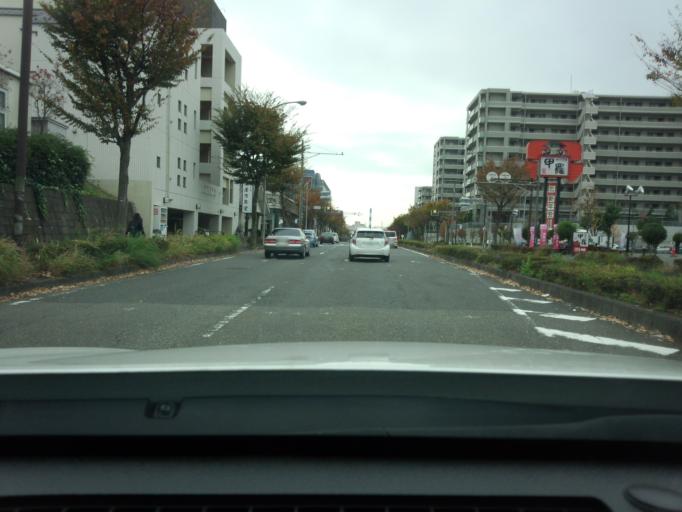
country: JP
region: Tokyo
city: Chofugaoka
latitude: 35.5575
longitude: 139.5781
